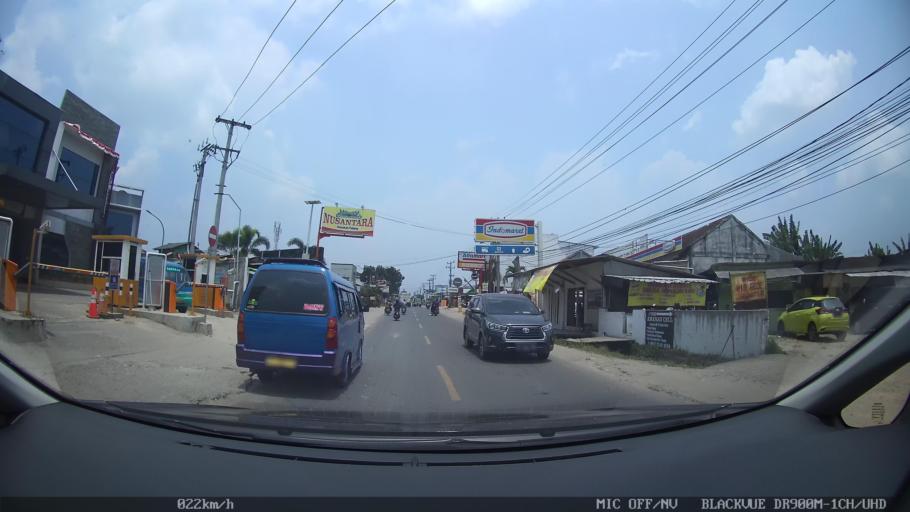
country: ID
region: Lampung
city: Pringsewu
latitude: -5.3590
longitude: 104.9907
